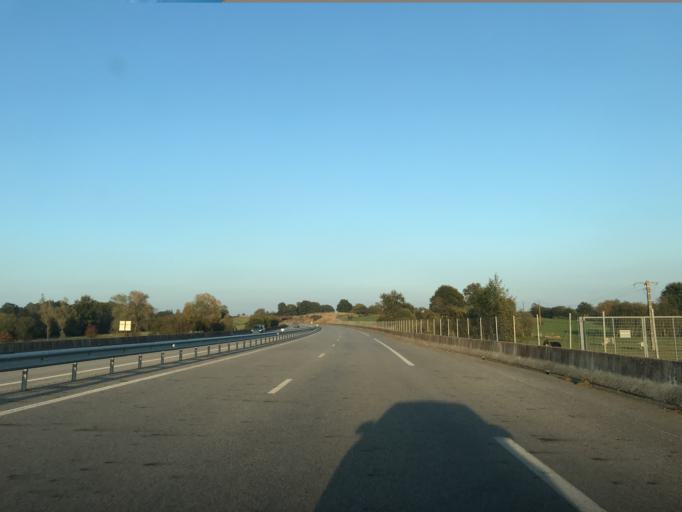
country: FR
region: Lower Normandy
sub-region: Departement de l'Orne
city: Sees
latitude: 48.4873
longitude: 0.2867
